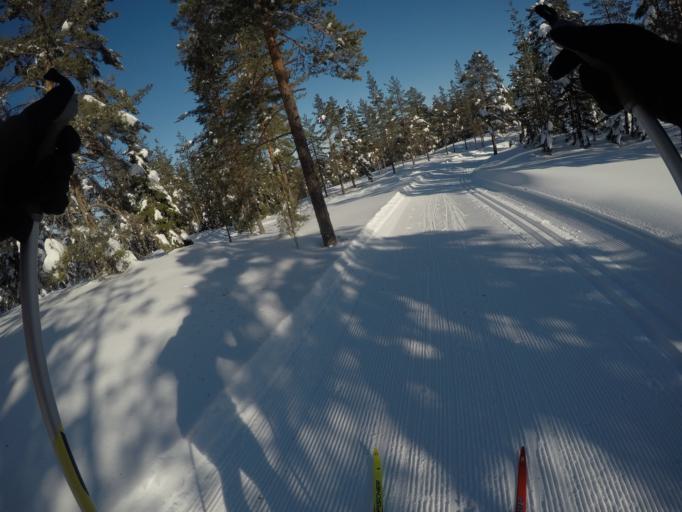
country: SE
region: Vaesternorrland
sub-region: Sundsvalls Kommun
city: Sundsvall
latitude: 62.3663
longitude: 17.2979
